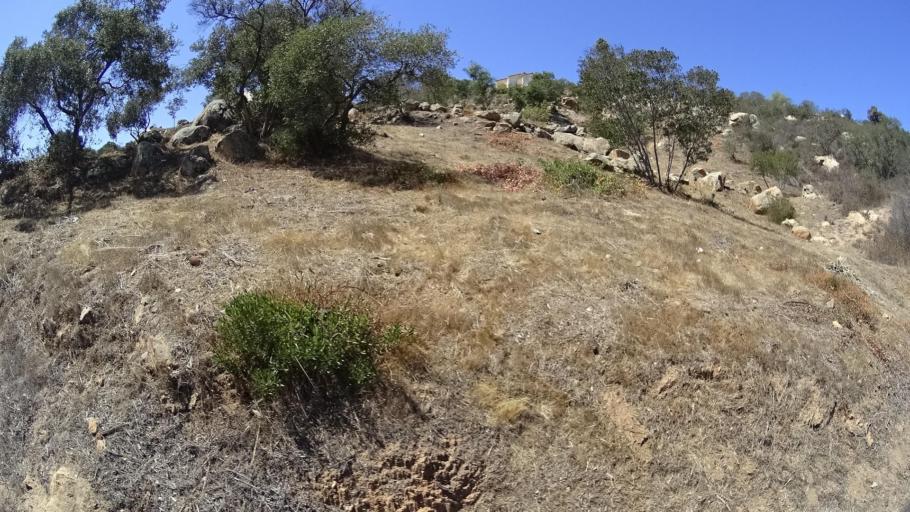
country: US
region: California
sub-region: San Diego County
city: Rainbow
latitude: 33.3854
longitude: -117.1284
